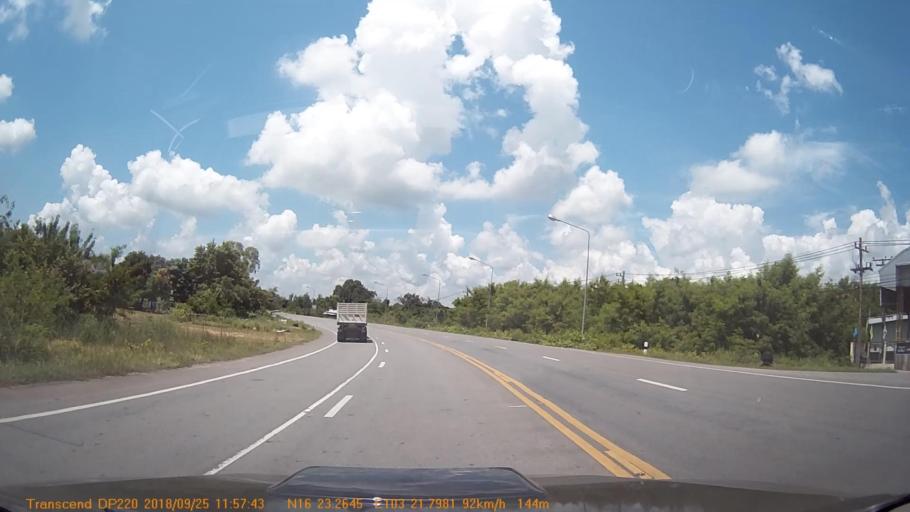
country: TH
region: Kalasin
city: Yang Talat
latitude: 16.3879
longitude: 103.3632
